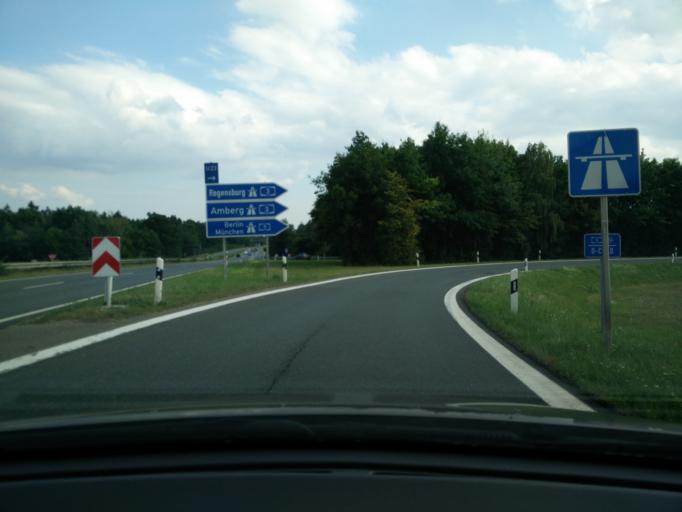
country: DE
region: Bavaria
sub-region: Regierungsbezirk Mittelfranken
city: Erlangen
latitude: 49.5370
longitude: 11.0311
